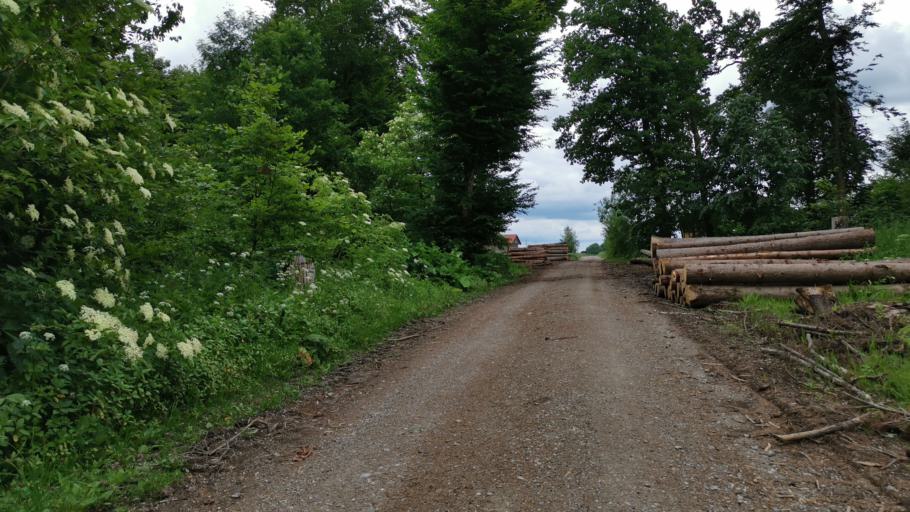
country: DE
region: Bavaria
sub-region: Upper Bavaria
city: Schaftlarn
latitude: 47.9994
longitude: 11.4408
